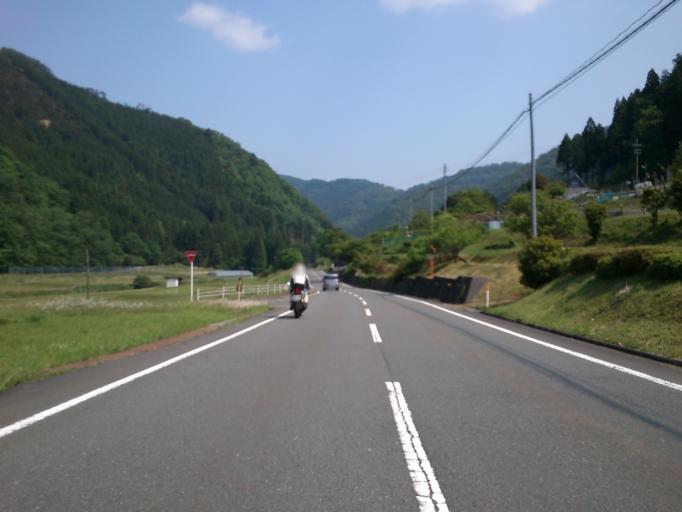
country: JP
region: Kyoto
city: Kameoka
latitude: 35.2405
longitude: 135.5609
